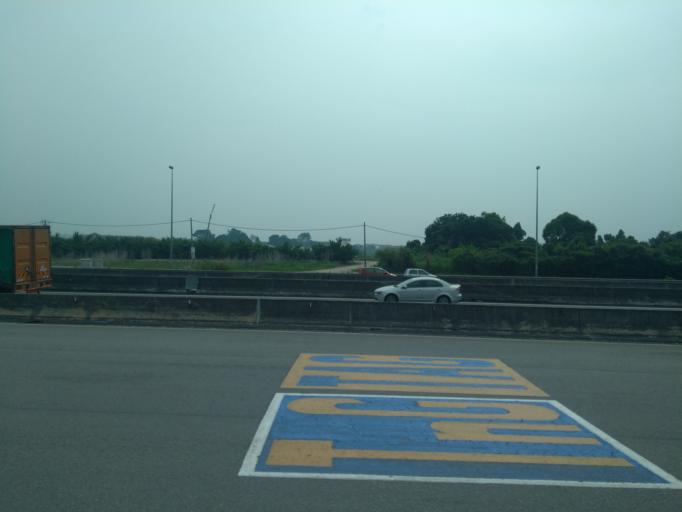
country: MY
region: Perak
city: Ipoh
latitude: 4.5875
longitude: 101.1447
